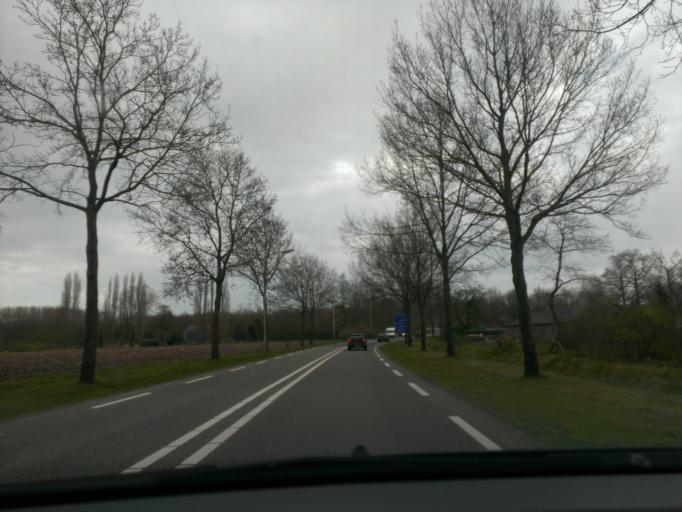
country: NL
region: Gelderland
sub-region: Gemeente Epe
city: Vaassen
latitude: 52.2924
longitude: 6.0033
